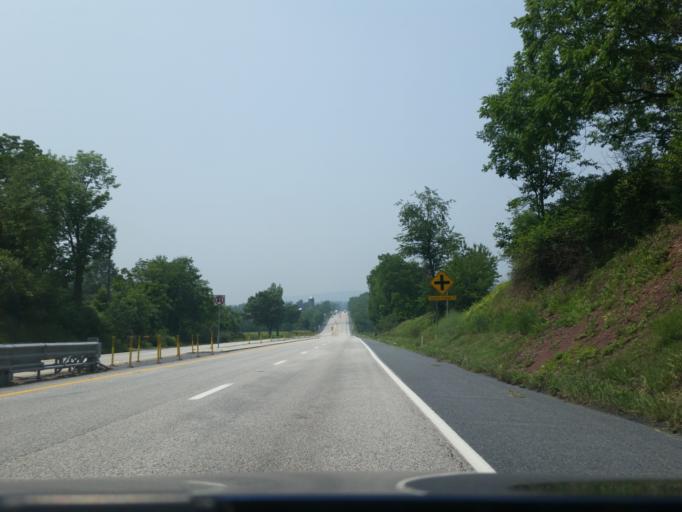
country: US
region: Pennsylvania
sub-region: Lebanon County
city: Jonestown
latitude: 40.4068
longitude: -76.5478
